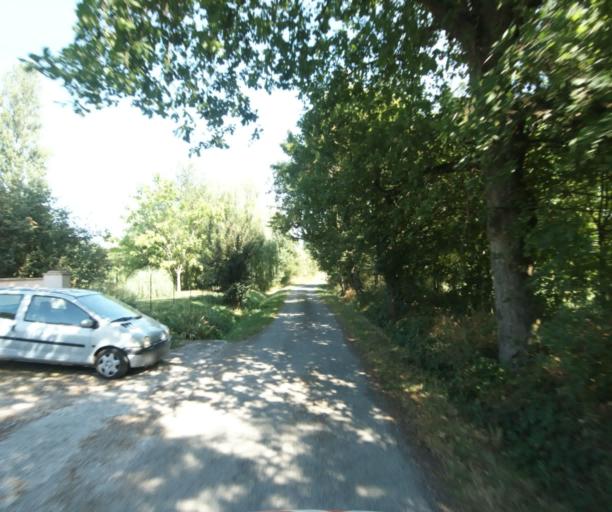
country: FR
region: Midi-Pyrenees
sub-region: Departement de la Haute-Garonne
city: Revel
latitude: 43.4977
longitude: 1.9709
